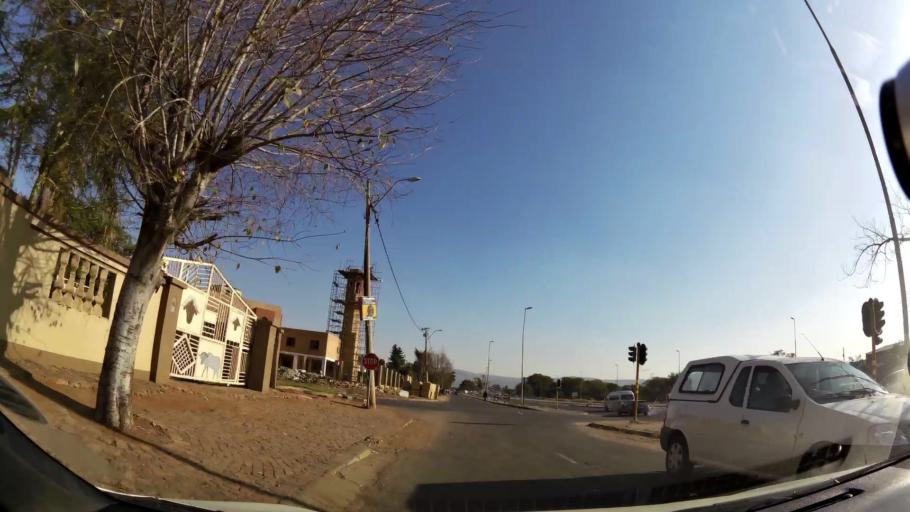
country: ZA
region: North-West
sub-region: Bojanala Platinum District Municipality
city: Rustenburg
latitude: -25.6517
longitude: 27.2499
